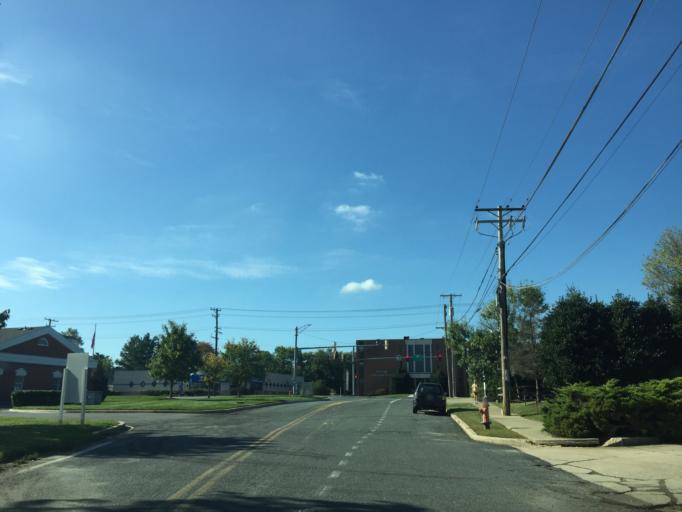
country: US
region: Maryland
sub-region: Baltimore County
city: Perry Hall
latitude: 39.4166
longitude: -76.4580
